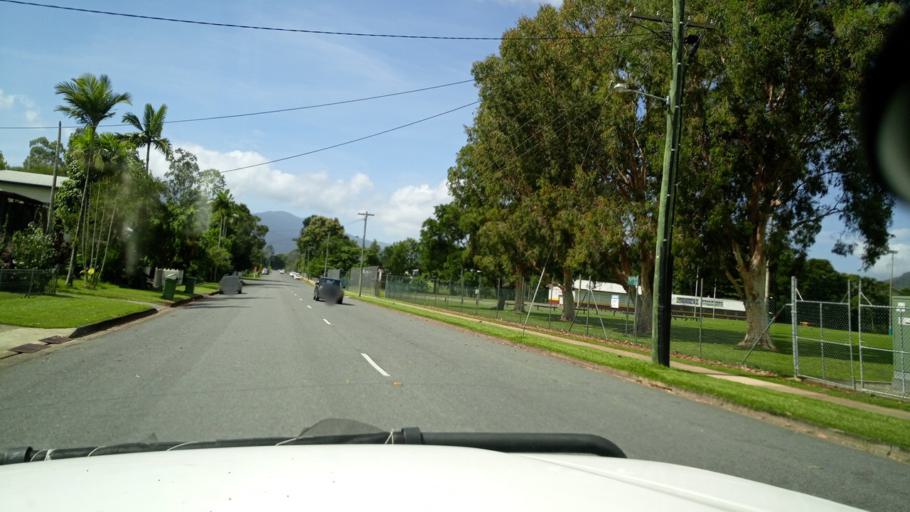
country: AU
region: Queensland
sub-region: Cairns
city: Woree
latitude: -17.0889
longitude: 145.7815
